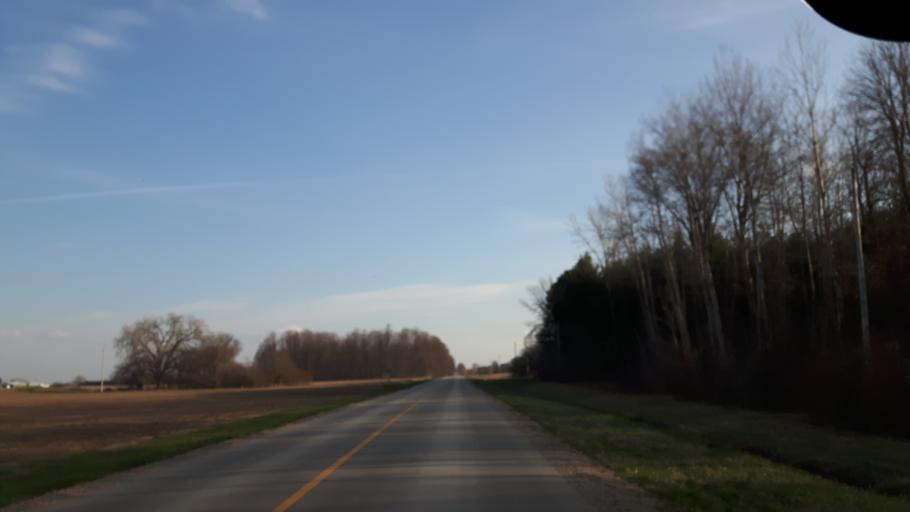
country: CA
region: Ontario
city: Goderich
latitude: 43.6539
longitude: -81.6643
